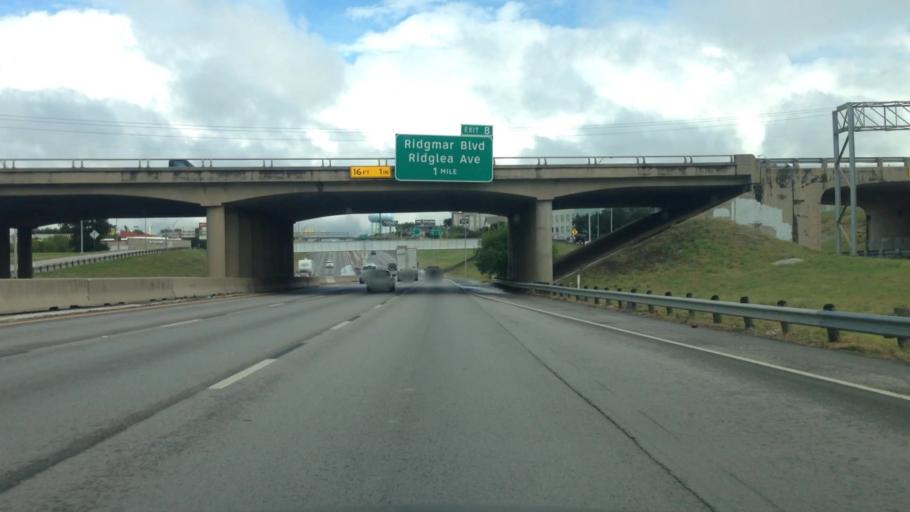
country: US
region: Texas
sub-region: Tarrant County
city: White Settlement
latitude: 32.7366
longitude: -97.4414
